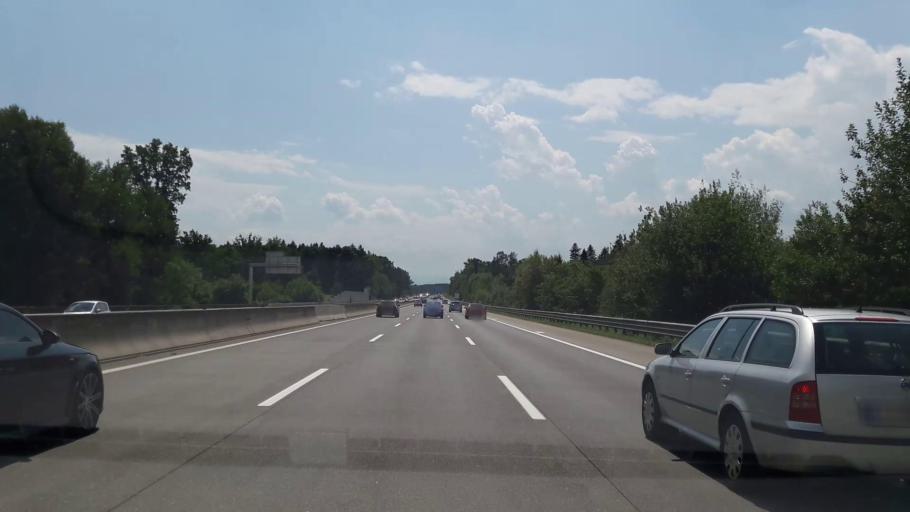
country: AT
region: Upper Austria
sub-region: Wels-Land
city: Marchtrenk
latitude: 48.1671
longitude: 14.1683
